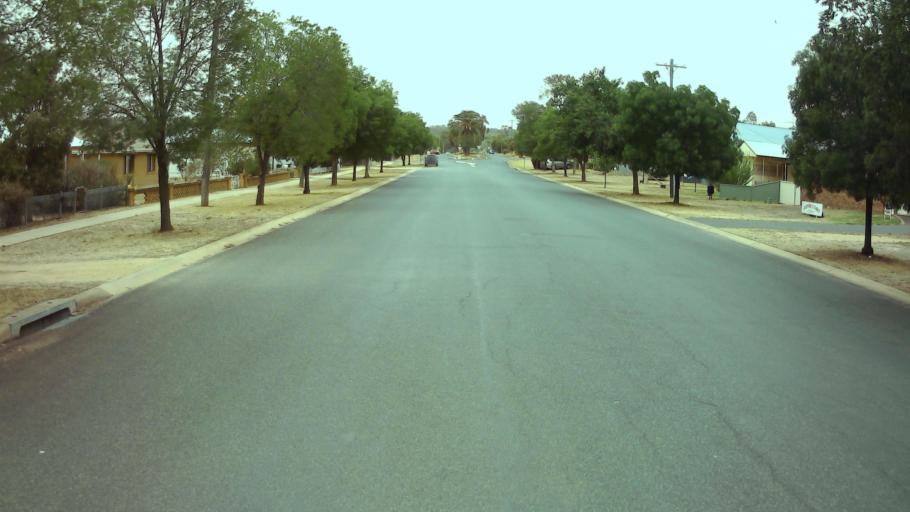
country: AU
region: New South Wales
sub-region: Weddin
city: Grenfell
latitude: -33.8969
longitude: 148.1654
